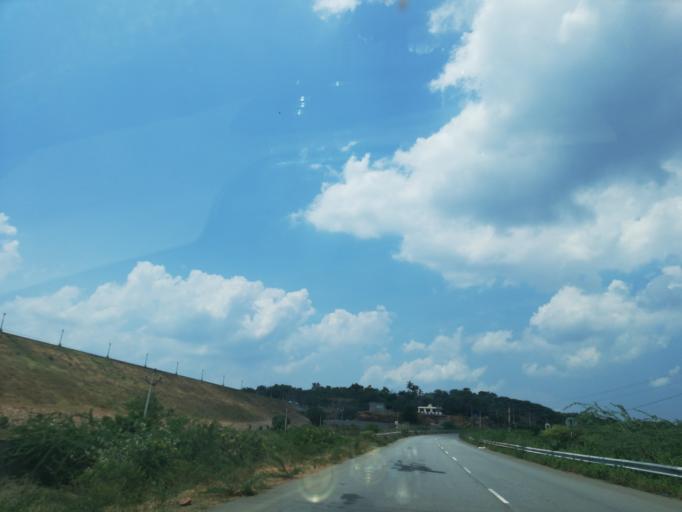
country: IN
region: Andhra Pradesh
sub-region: Guntur
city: Macherla
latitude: 16.5973
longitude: 79.3077
